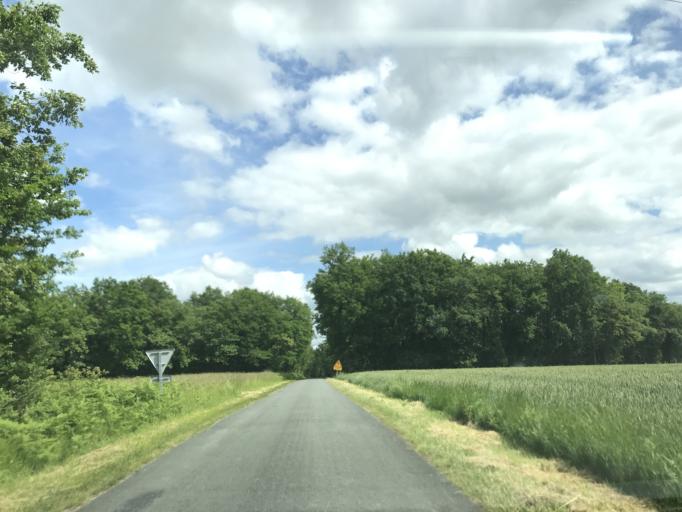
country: FR
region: Poitou-Charentes
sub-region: Departement de la Charente
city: Chalais
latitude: 45.2778
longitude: 0.1047
